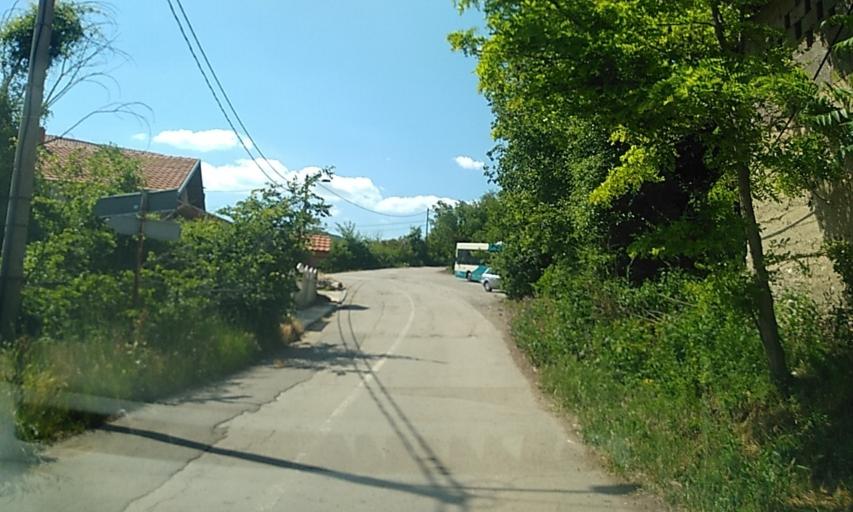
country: RS
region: Central Serbia
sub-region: Nisavski Okrug
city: Niska Banja
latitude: 43.3660
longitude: 21.9955
